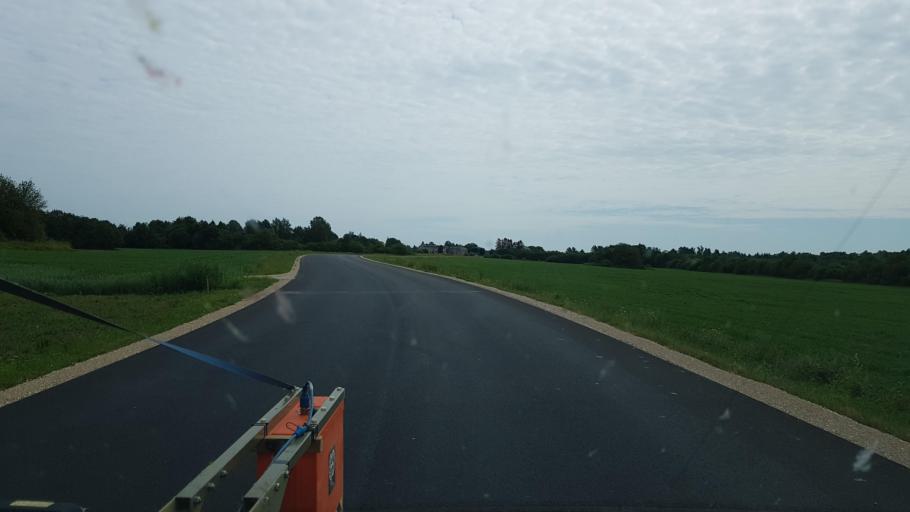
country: EE
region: Paernumaa
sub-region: Halinga vald
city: Parnu-Jaagupi
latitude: 58.6231
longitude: 24.3779
